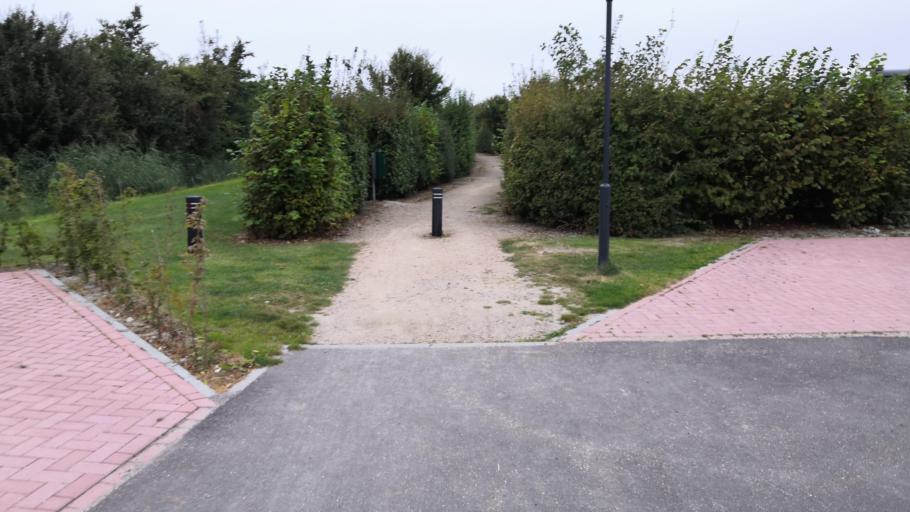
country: NL
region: Zeeland
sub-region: Gemeente Middelburg
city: Middelburg
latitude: 51.5564
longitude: 3.5147
